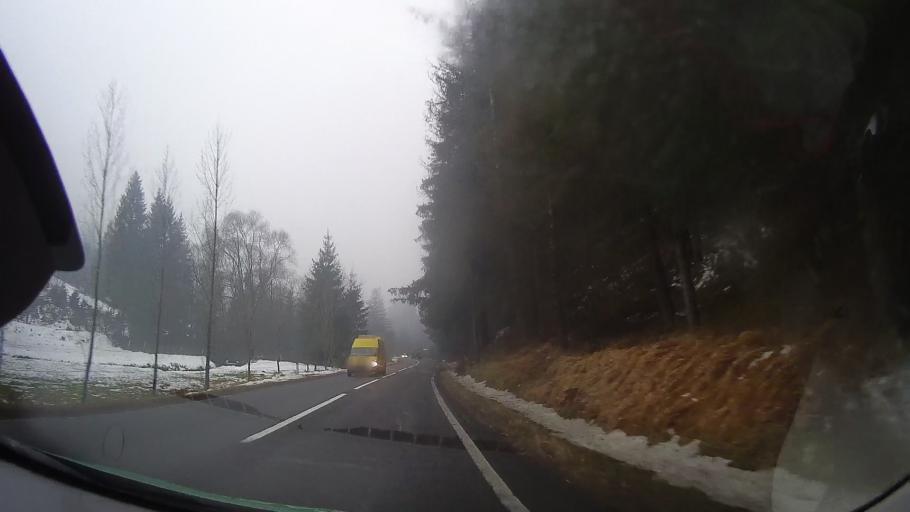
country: RO
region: Harghita
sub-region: Municipiul Gheorgheni
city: Gheorgheni
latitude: 46.7499
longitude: 25.6857
